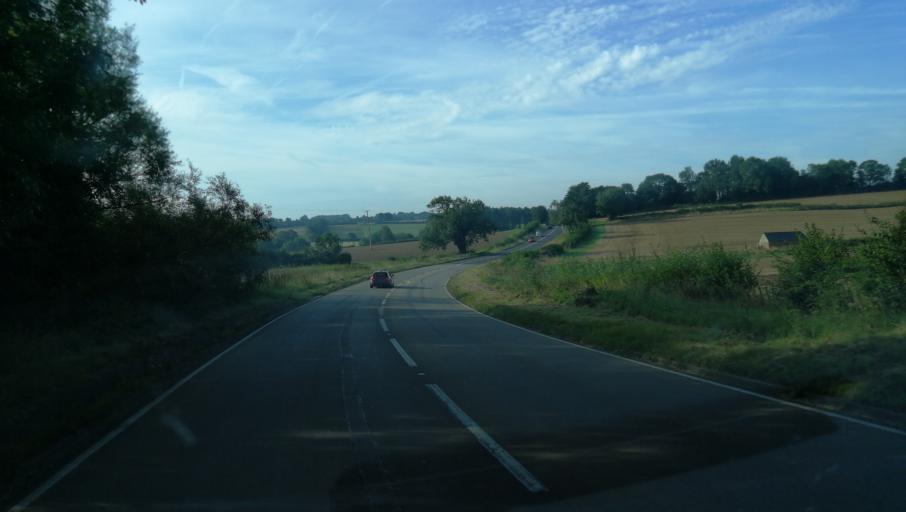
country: GB
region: England
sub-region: Oxfordshire
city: Deddington
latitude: 51.9746
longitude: -1.3178
